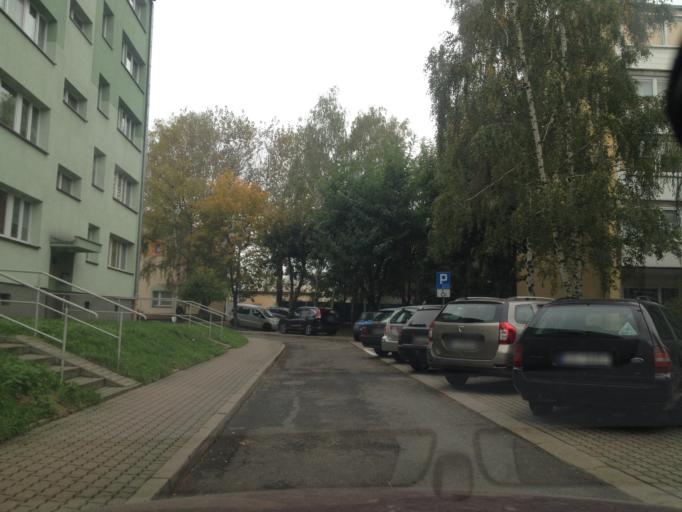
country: PL
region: Lower Silesian Voivodeship
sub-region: Powiat zgorzelecki
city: Zgorzelec
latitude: 51.1571
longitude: 15.0135
